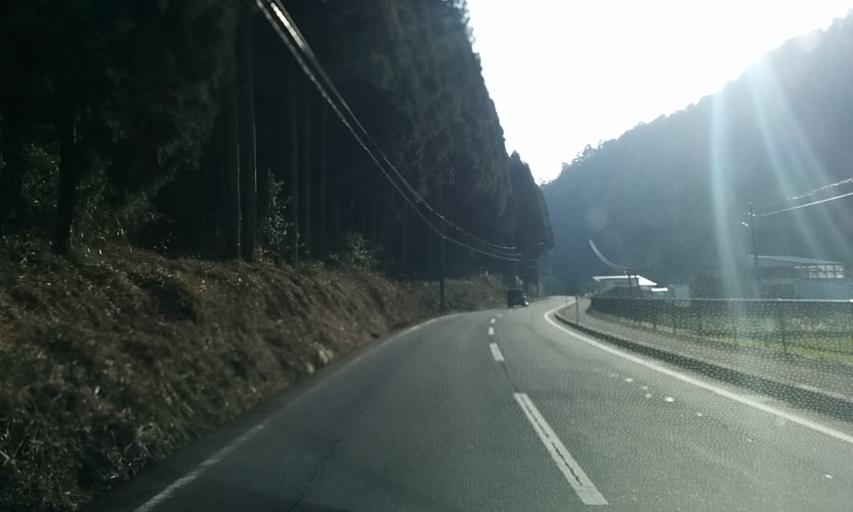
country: JP
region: Fukui
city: Obama
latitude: 35.2953
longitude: 135.6026
